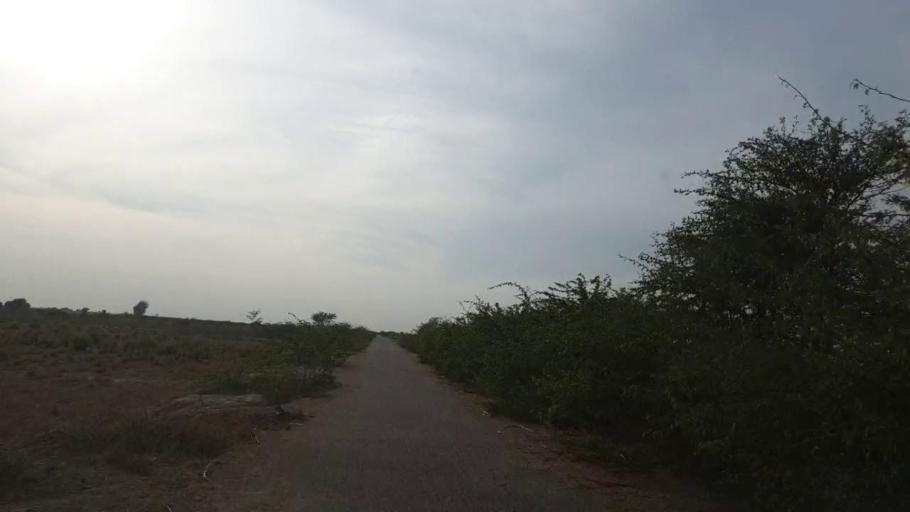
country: PK
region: Sindh
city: Nabisar
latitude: 24.9975
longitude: 69.5213
